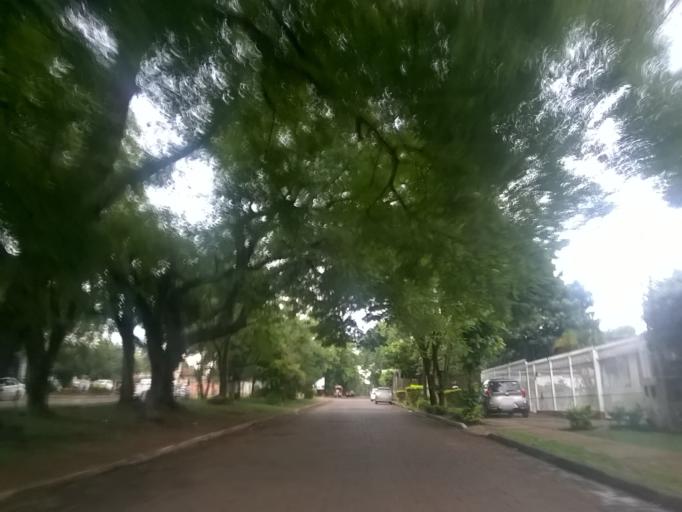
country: PY
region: Alto Parana
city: Presidente Franco
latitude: -25.5366
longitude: -54.6270
